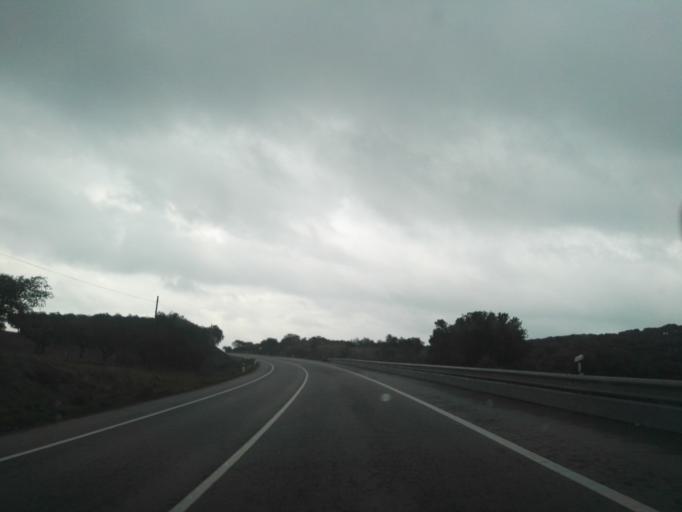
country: PT
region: Portalegre
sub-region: Portalegre
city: Alegrete
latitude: 39.1764
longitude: -7.3400
